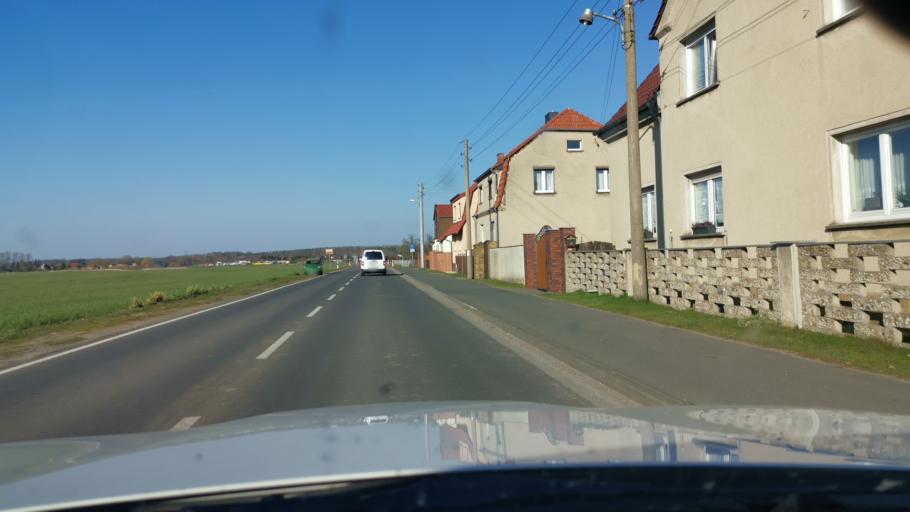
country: DE
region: Saxony-Anhalt
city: Jessnitz
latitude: 51.7134
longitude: 12.3104
